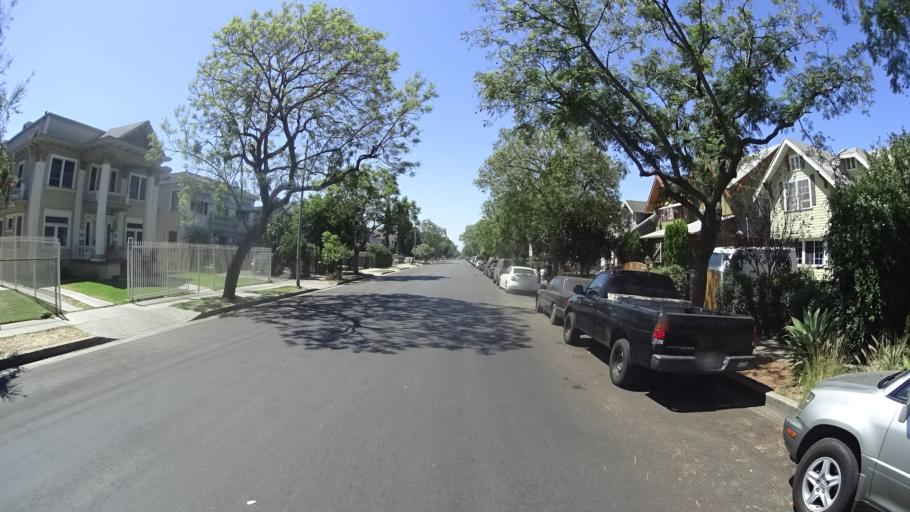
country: US
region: California
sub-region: Los Angeles County
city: Los Angeles
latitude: 34.0308
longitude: -118.2981
